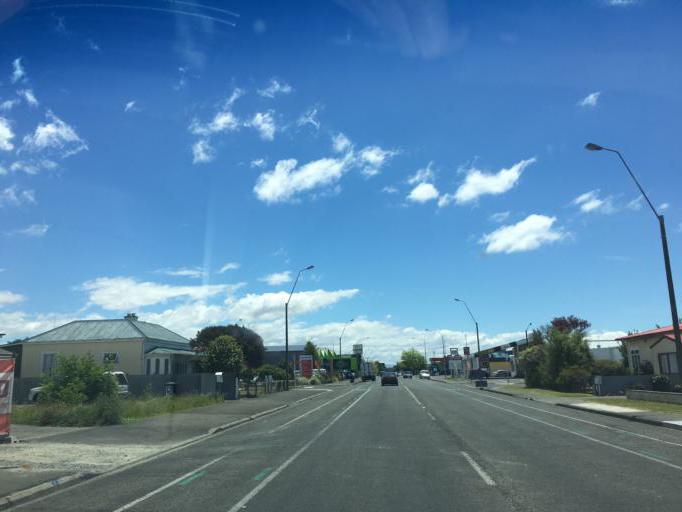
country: NZ
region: Hawke's Bay
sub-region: Hastings District
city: Hastings
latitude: -39.6441
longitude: 176.8510
